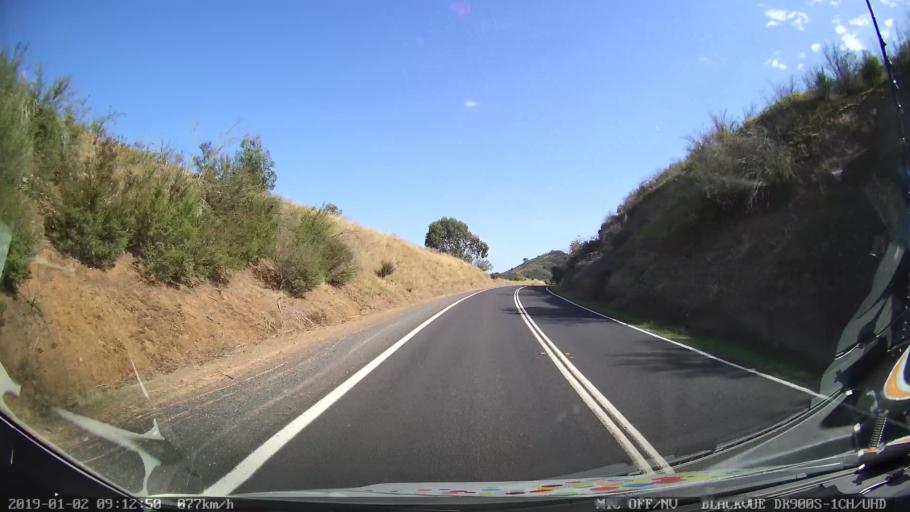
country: AU
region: New South Wales
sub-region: Tumut Shire
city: Tumut
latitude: -35.4956
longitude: 148.2700
